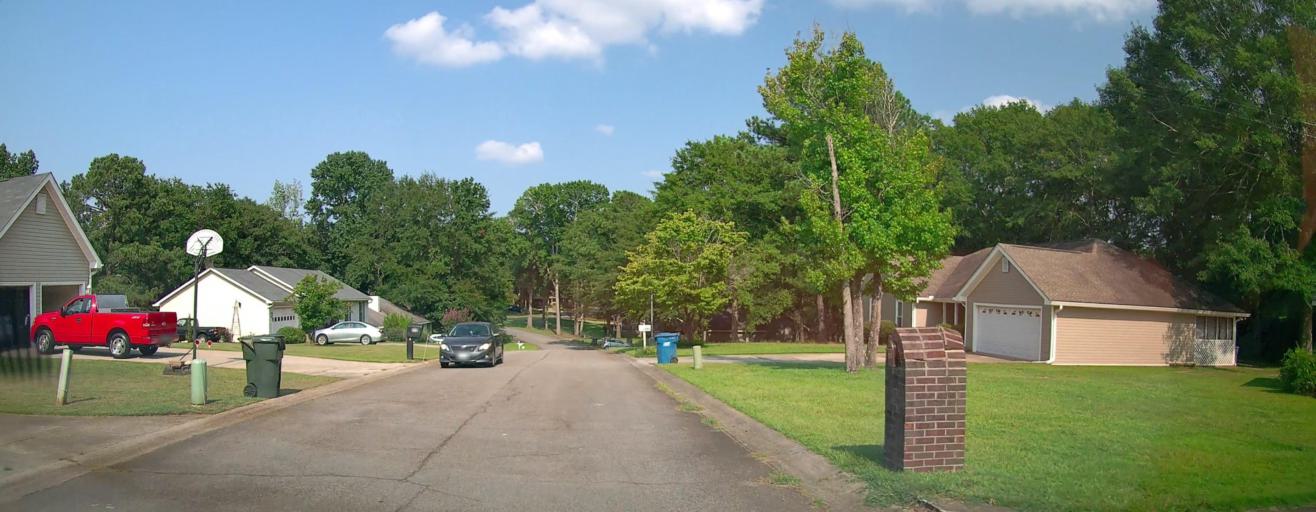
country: US
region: Georgia
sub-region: Houston County
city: Centerville
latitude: 32.6437
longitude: -83.6953
